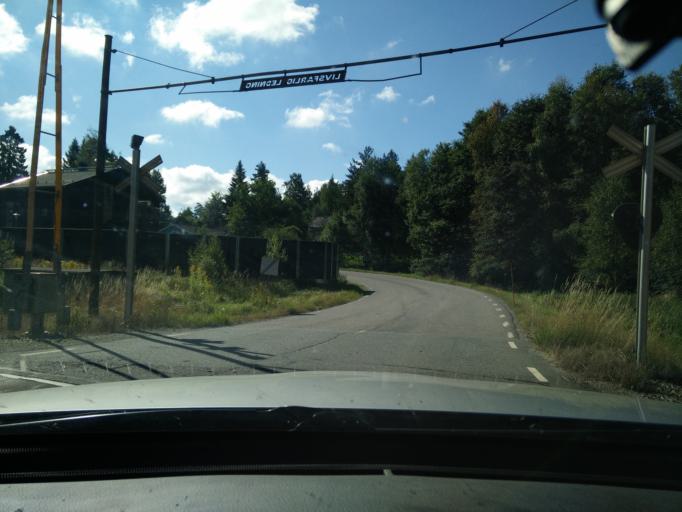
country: SE
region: Stockholm
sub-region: Lidingo
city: Lidingoe
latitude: 59.4661
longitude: 18.1808
